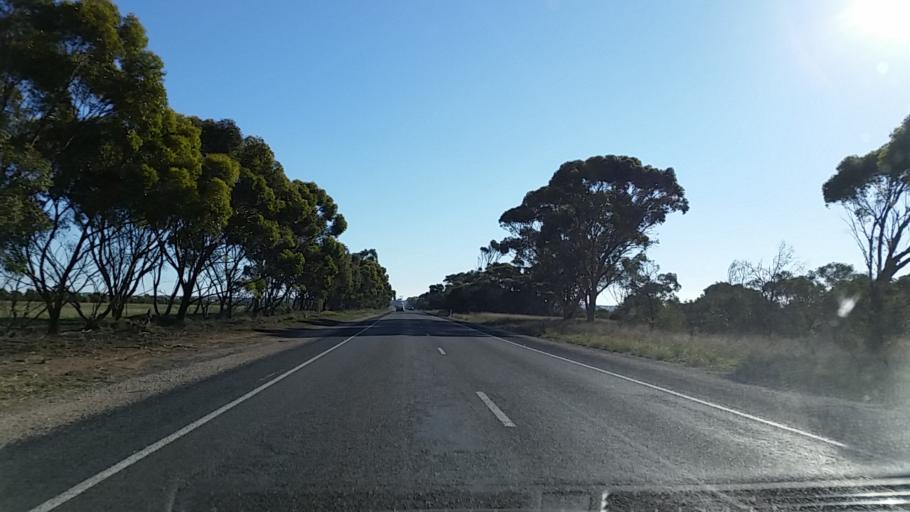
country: AU
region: South Australia
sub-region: Mount Barker
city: Callington
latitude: -35.1174
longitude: 139.1239
